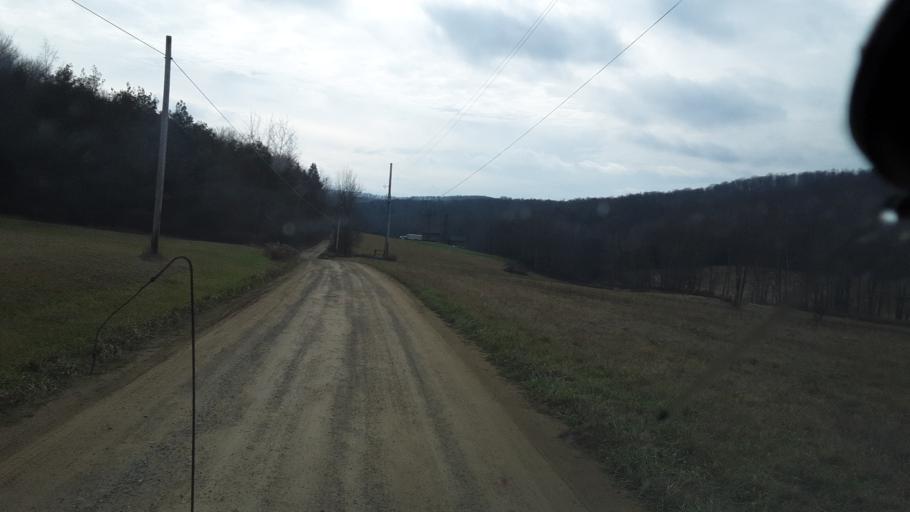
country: US
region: Pennsylvania
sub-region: Tioga County
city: Westfield
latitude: 41.9179
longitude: -77.7183
